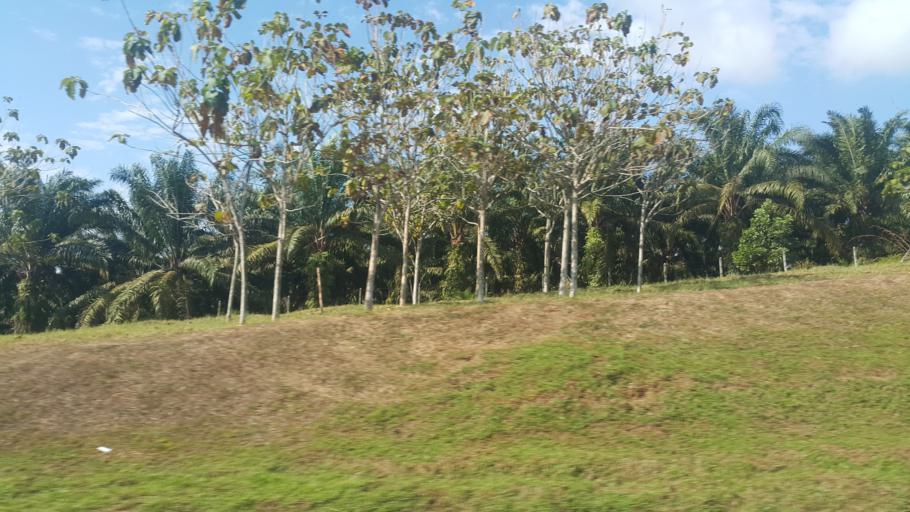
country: MY
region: Johor
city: Kelapa Sawit
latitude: 1.7313
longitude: 103.4200
